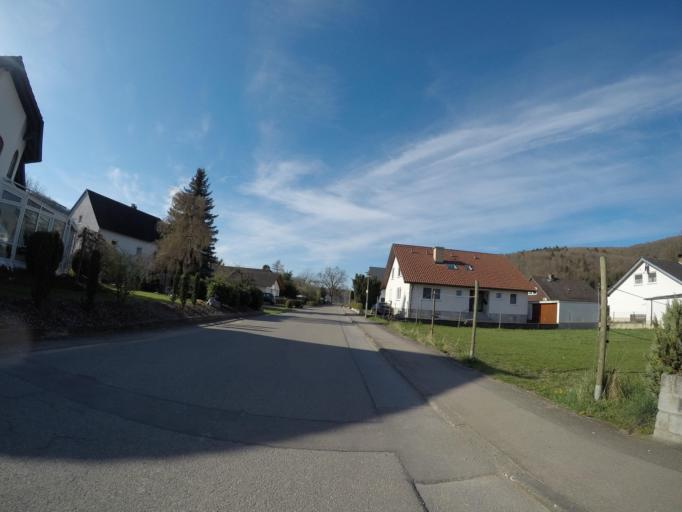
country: DE
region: Baden-Wuerttemberg
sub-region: Tuebingen Region
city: Schelklingen
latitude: 48.3602
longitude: 9.7152
